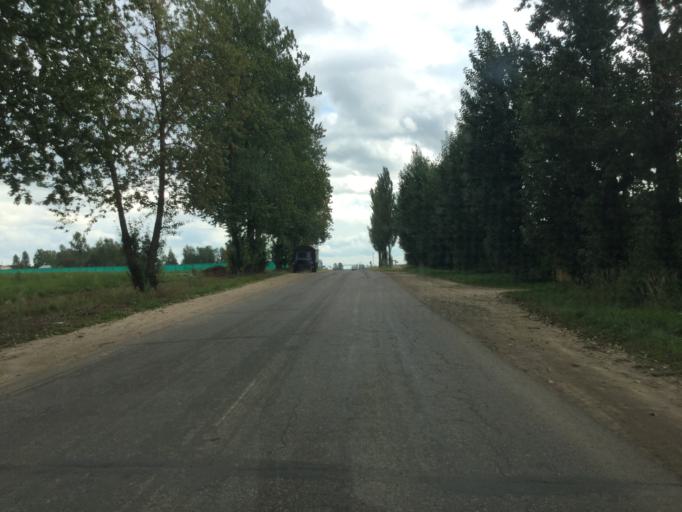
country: BY
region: Vitebsk
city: Vitebsk
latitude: 55.1618
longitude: 30.2600
